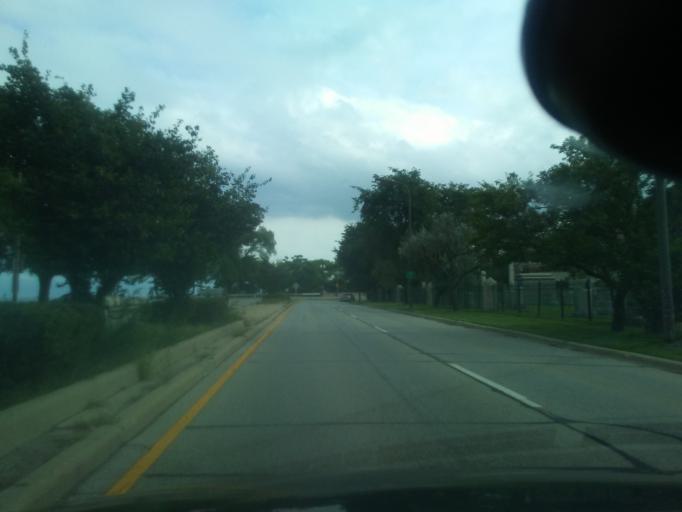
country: US
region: Illinois
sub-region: Cook County
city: Evanston
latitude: 42.0240
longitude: -87.6659
